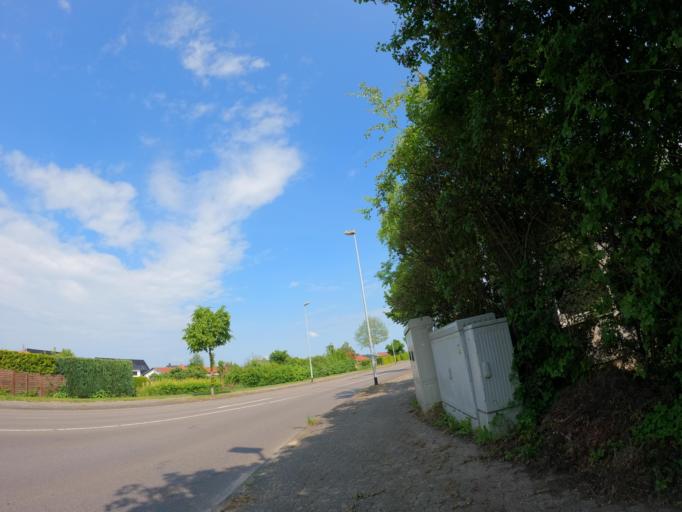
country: DE
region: Mecklenburg-Vorpommern
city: Stralsund
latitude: 54.2893
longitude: 13.0531
